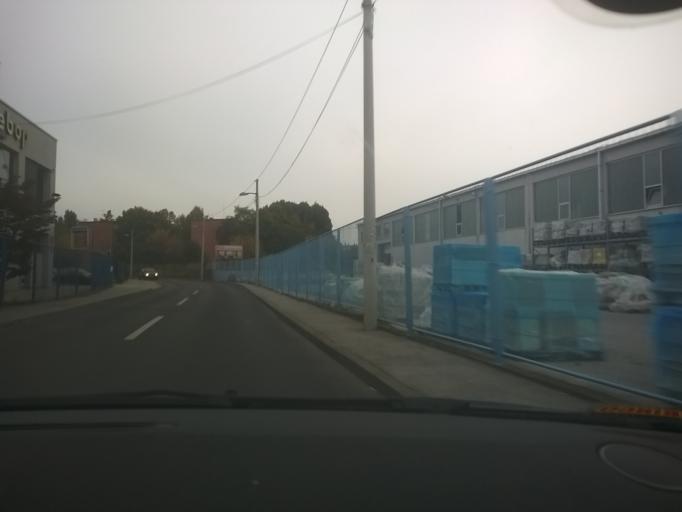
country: HR
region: Grad Zagreb
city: Jankomir
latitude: 45.8042
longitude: 15.9234
